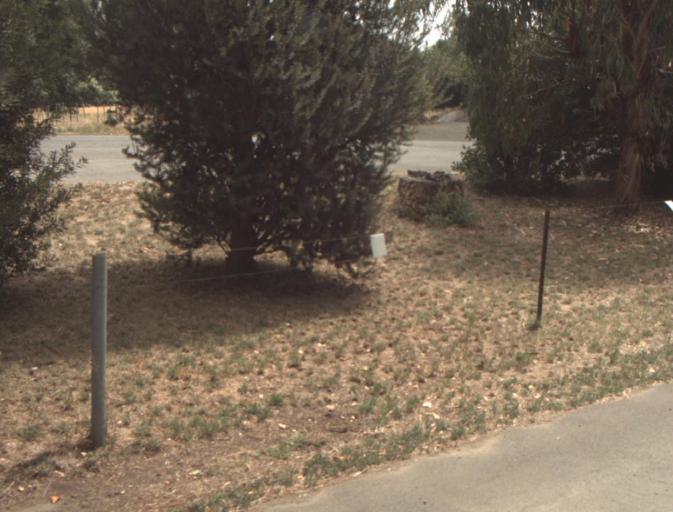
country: AU
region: Tasmania
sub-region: Launceston
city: Newstead
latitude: -41.4395
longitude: 147.1729
